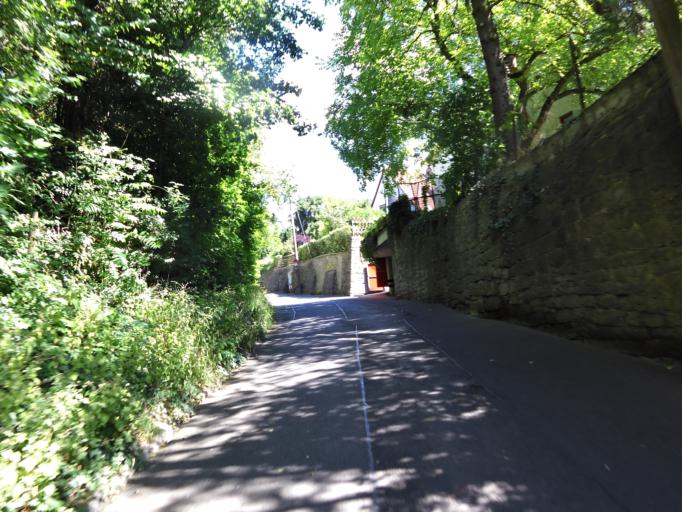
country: DE
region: Bavaria
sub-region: Regierungsbezirk Unterfranken
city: Wuerzburg
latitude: 49.8053
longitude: 9.9417
